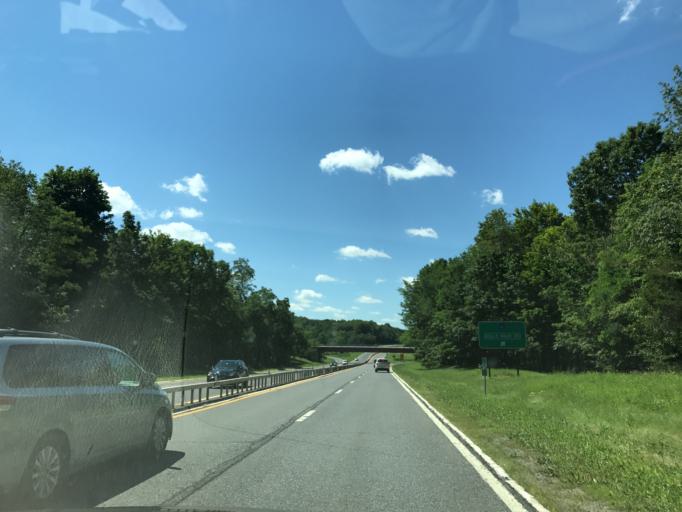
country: US
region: New York
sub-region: Dutchess County
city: Pine Plains
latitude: 41.9150
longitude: -73.7679
